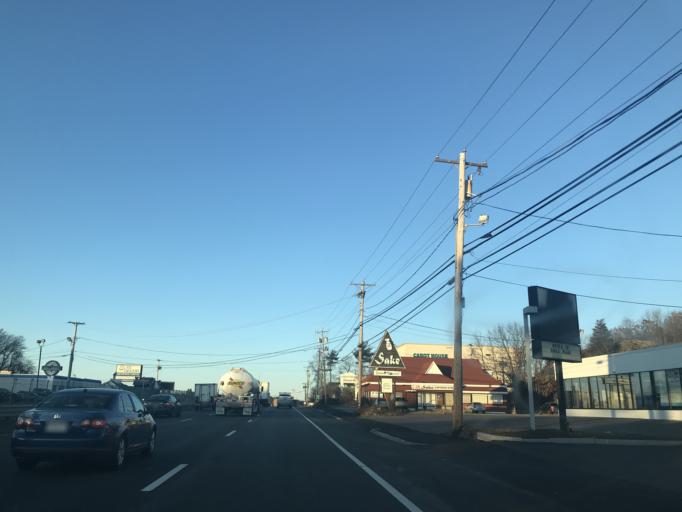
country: US
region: Massachusetts
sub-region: Essex County
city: Saugus
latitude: 42.4746
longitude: -71.0238
